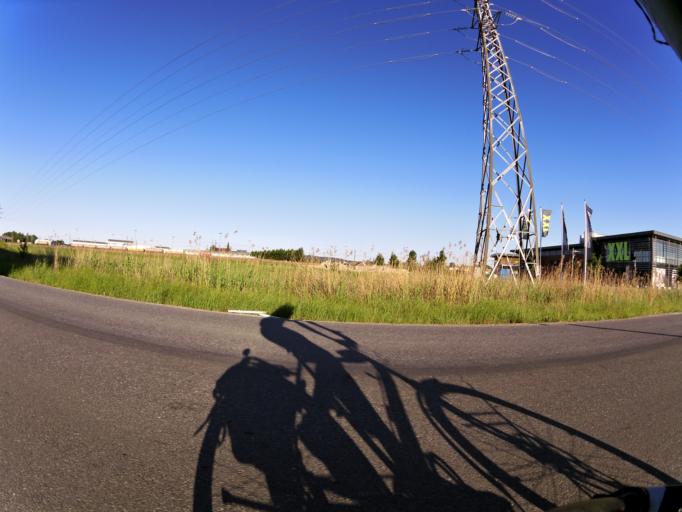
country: NO
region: Ostfold
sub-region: Fredrikstad
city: Fredrikstad
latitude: 59.2571
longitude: 11.0030
